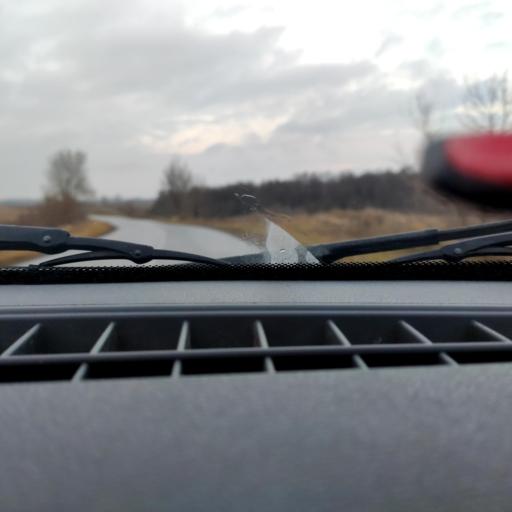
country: RU
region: Bashkortostan
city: Avdon
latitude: 54.5092
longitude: 55.8390
